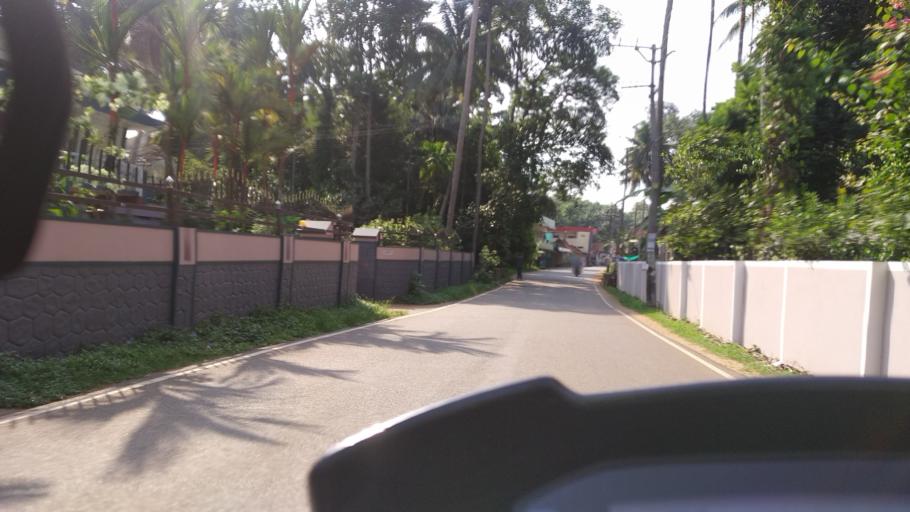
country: IN
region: Kerala
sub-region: Ernakulam
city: Piravam
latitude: 9.8667
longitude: 76.5067
